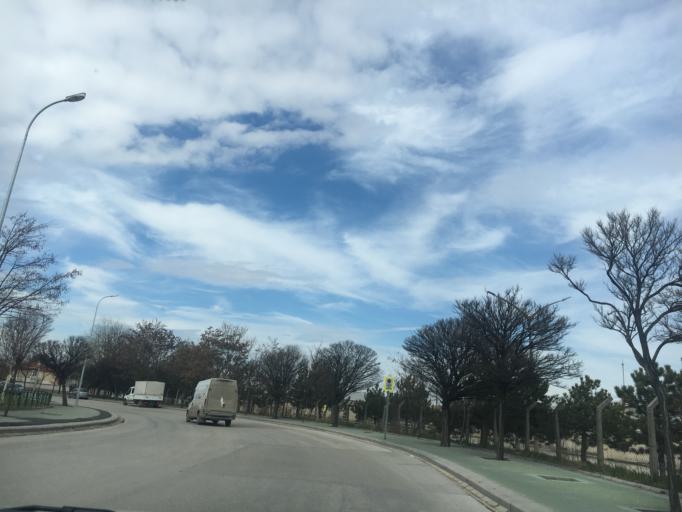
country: TR
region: Eskisehir
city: Eskisehir
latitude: 39.7797
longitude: 30.5336
